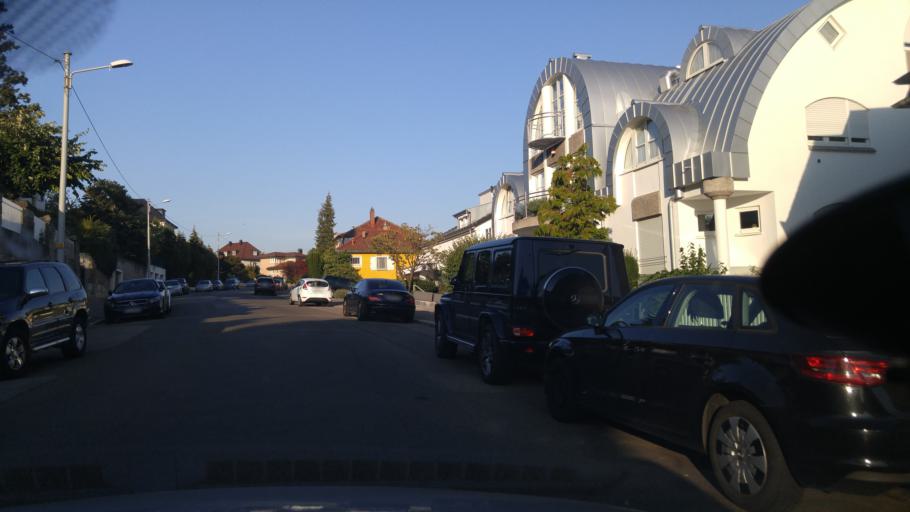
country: DE
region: Baden-Wuerttemberg
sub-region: Regierungsbezirk Stuttgart
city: Stuttgart
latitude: 48.7926
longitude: 9.1693
